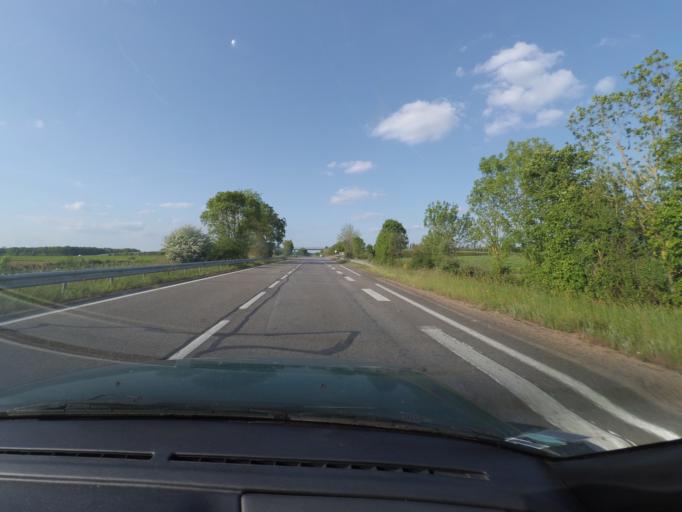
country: FR
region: Pays de la Loire
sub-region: Departement de la Vendee
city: Saligny
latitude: 46.8540
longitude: -1.4105
